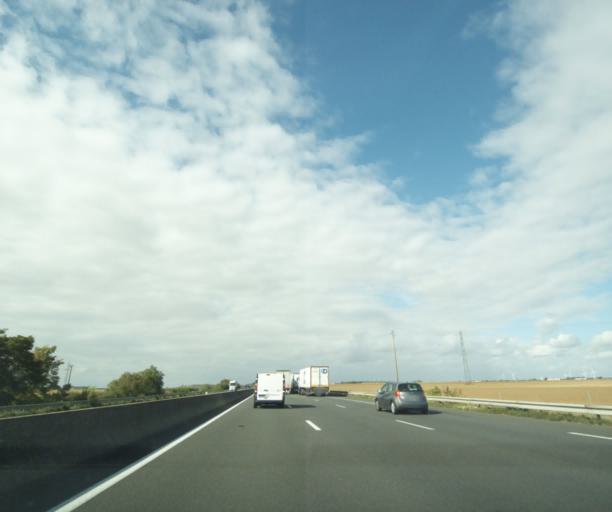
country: FR
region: Centre
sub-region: Departement d'Eure-et-Loir
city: Janville
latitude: 48.1807
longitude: 1.8542
